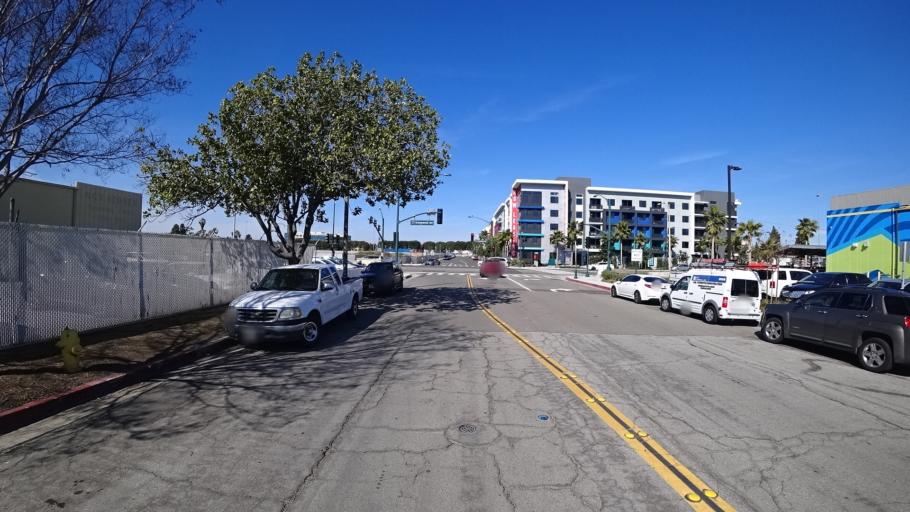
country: US
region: California
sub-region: Orange County
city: Orange
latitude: 33.7957
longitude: -117.8858
